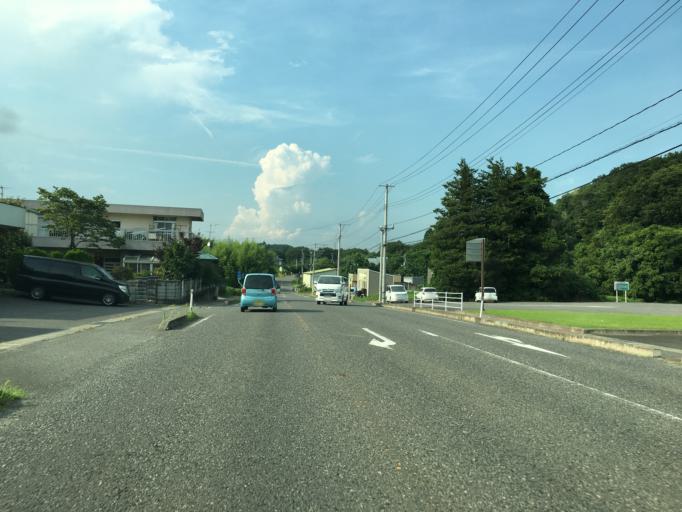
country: JP
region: Fukushima
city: Miharu
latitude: 37.4473
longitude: 140.4275
